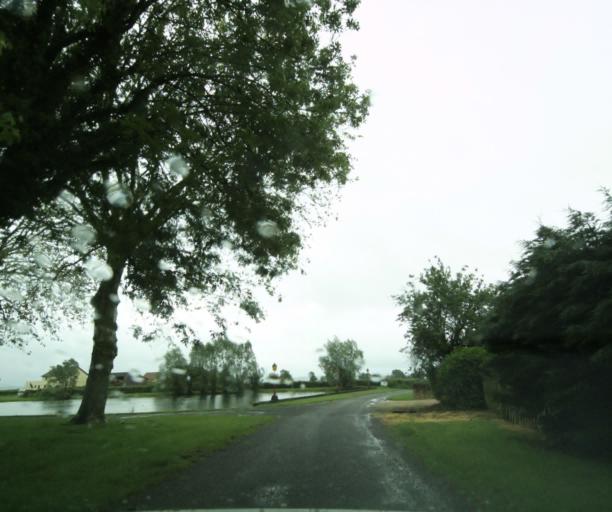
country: FR
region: Bourgogne
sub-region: Departement de Saone-et-Loire
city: Charolles
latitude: 46.4754
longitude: 4.2961
